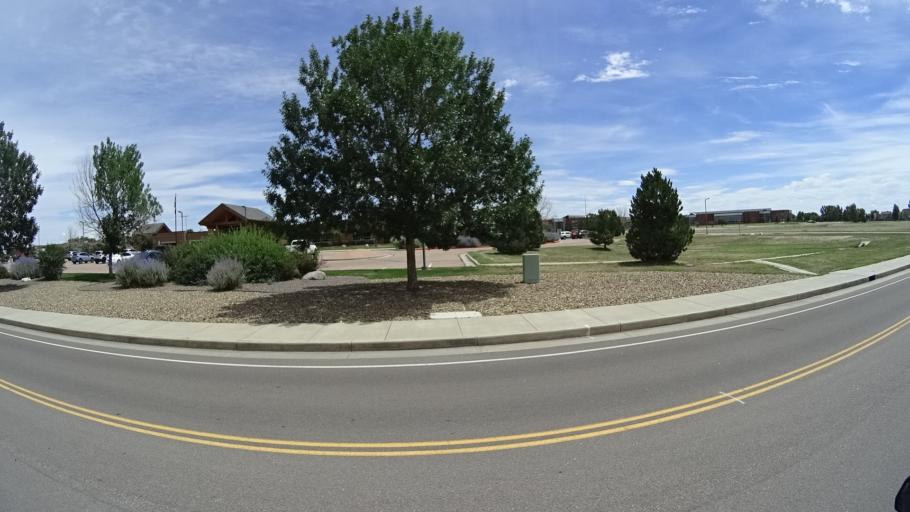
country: US
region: Colorado
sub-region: El Paso County
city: Fountain
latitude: 38.6754
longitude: -104.6873
